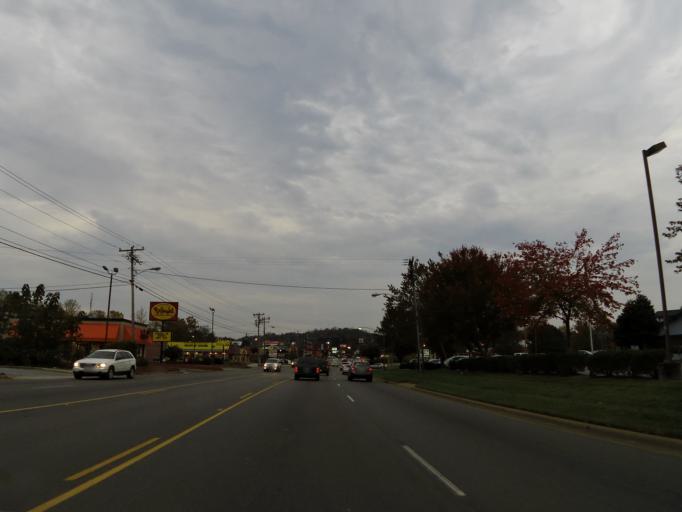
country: US
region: North Carolina
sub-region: Caldwell County
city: Lenoir
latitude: 35.9183
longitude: -81.5246
